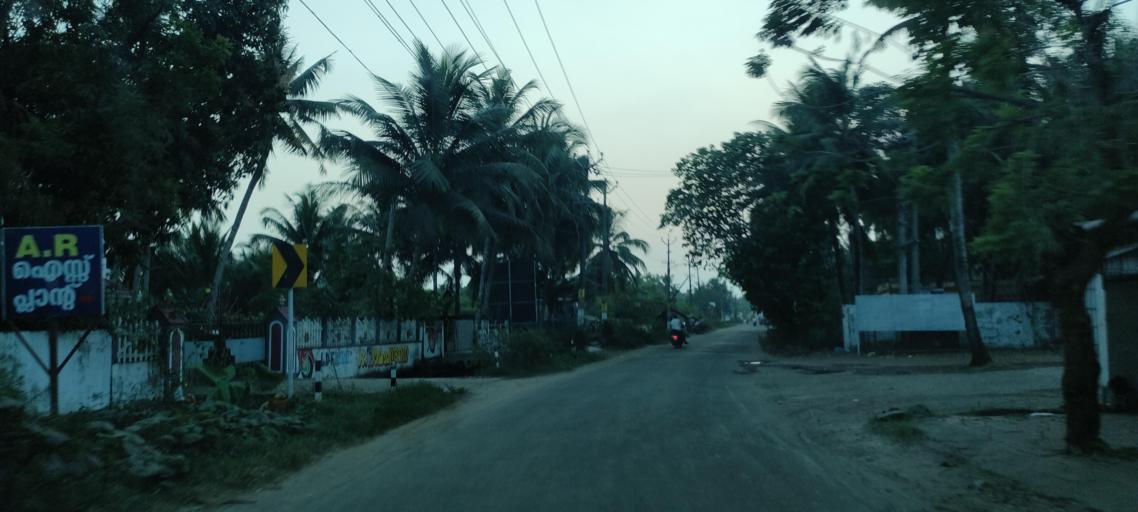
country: IN
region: Kerala
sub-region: Alappuzha
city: Kayankulam
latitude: 9.1173
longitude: 76.4829
